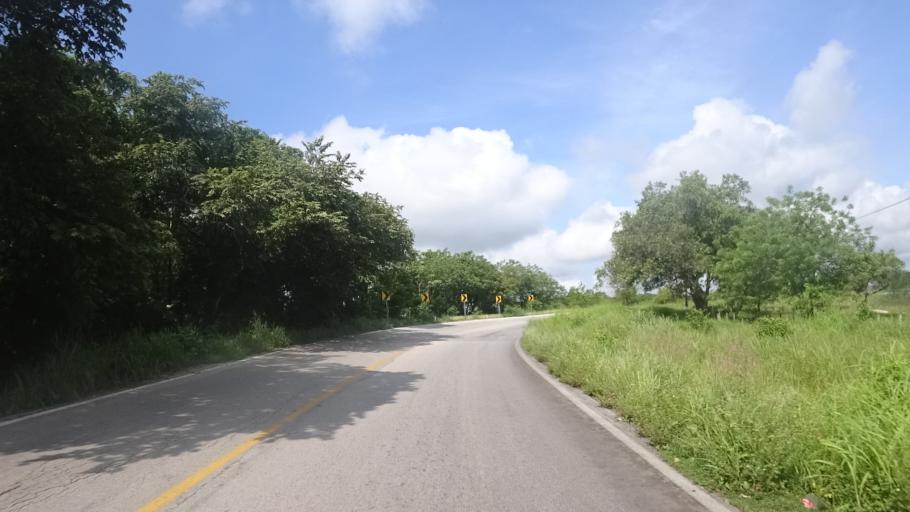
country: MX
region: Chiapas
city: Palenque
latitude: 17.5519
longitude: -91.9991
